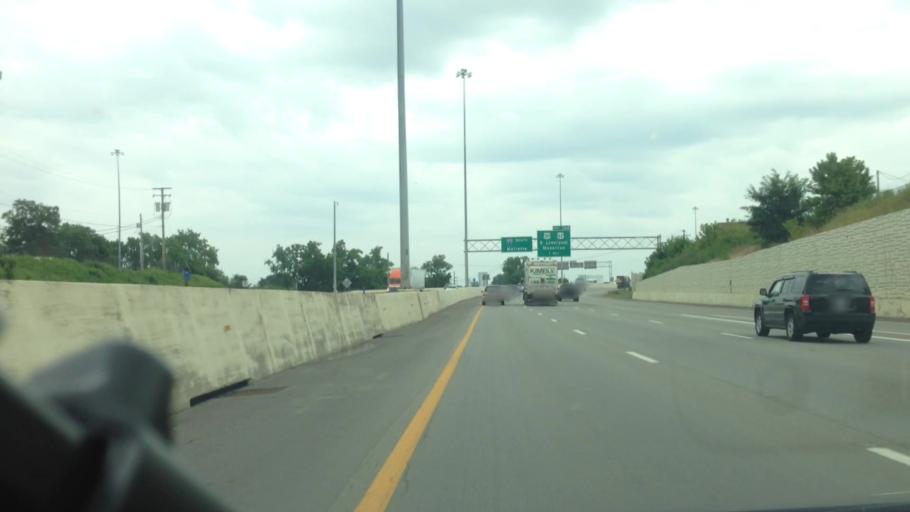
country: US
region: Ohio
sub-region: Stark County
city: Canton
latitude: 40.7988
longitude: -81.3936
